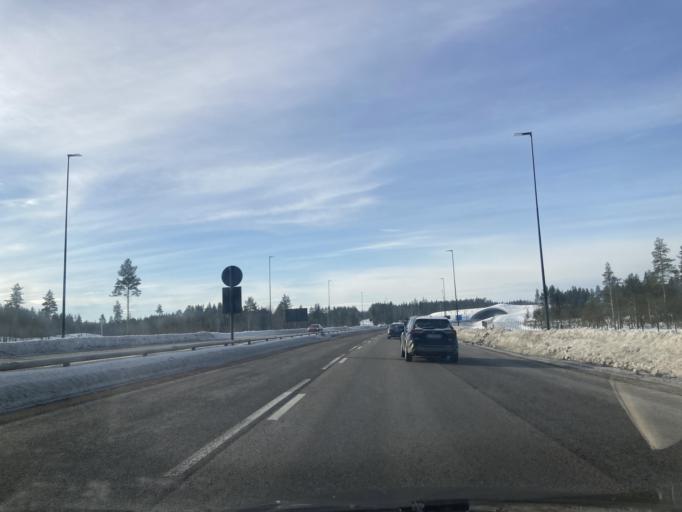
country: NO
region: Hedmark
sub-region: Elverum
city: Elverum
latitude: 60.8862
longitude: 11.5047
